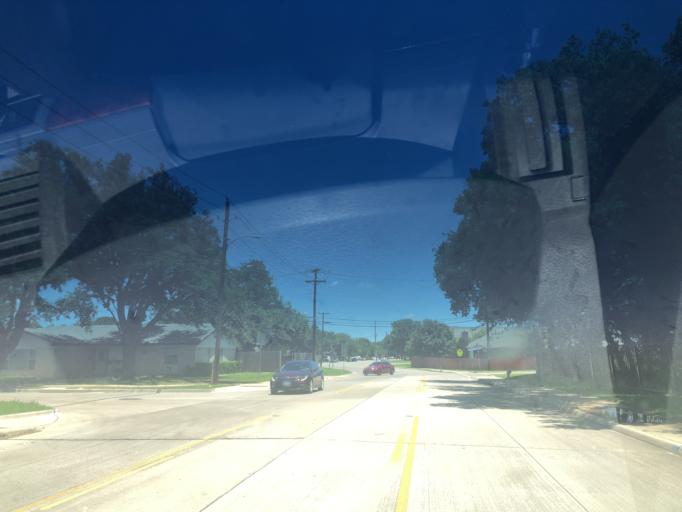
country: US
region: Texas
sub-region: Dallas County
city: Grand Prairie
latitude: 32.7133
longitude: -97.0032
